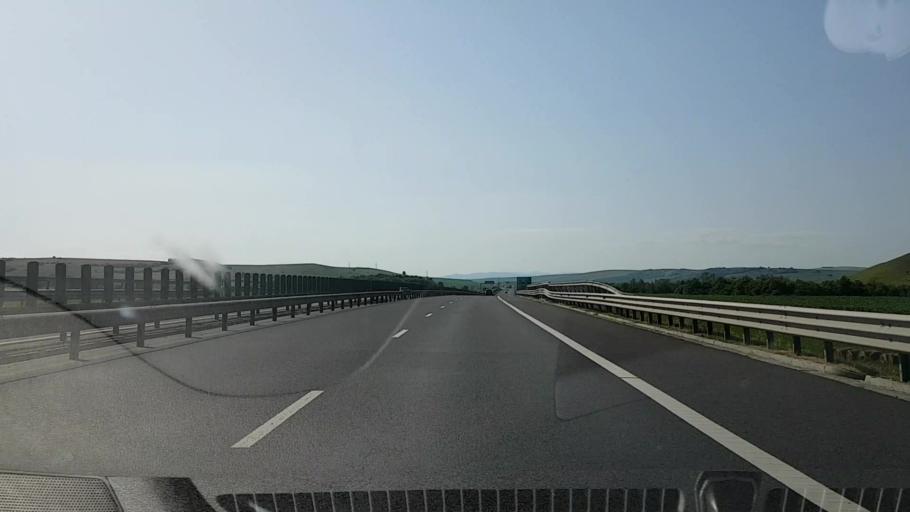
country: RO
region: Alba
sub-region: Comuna Garbova
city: Garbova
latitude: 45.9045
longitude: 23.7513
